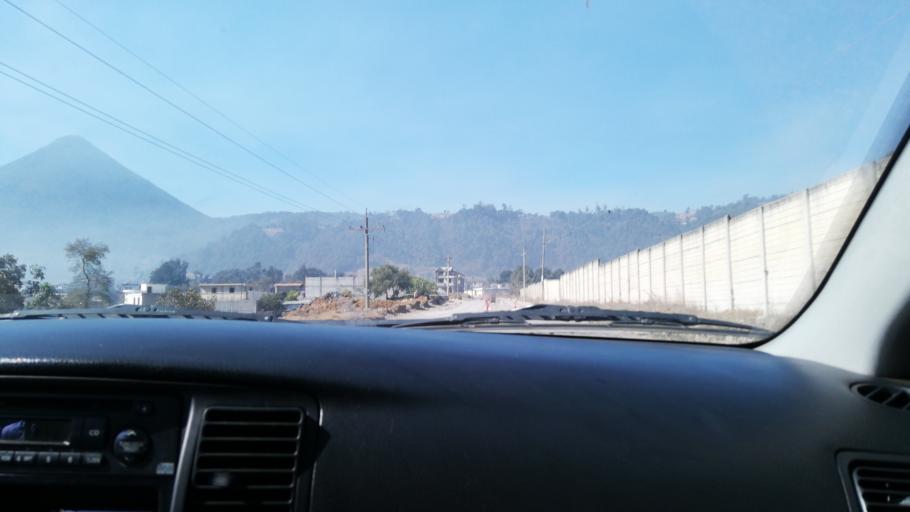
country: GT
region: Quetzaltenango
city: Quetzaltenango
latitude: 14.8106
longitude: -91.5509
